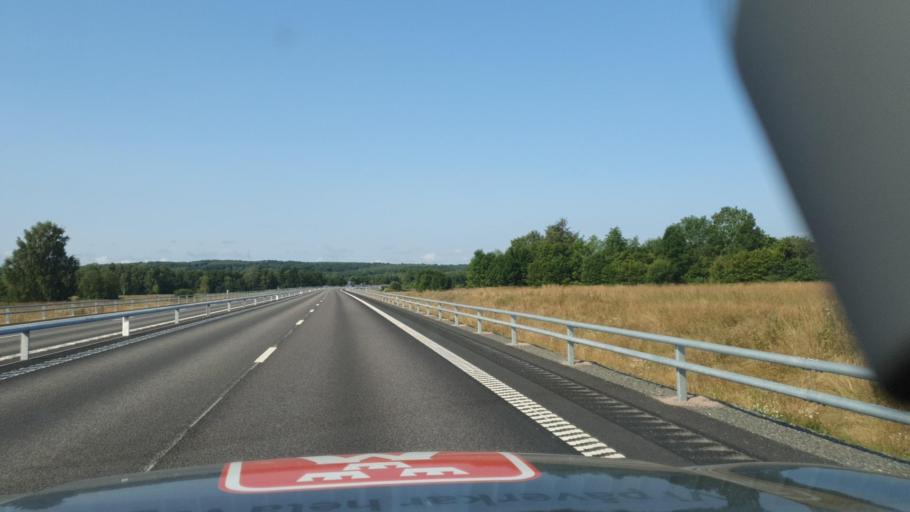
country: SE
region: Skane
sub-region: Kristianstads Kommun
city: Onnestad
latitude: 55.9553
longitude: 13.9226
